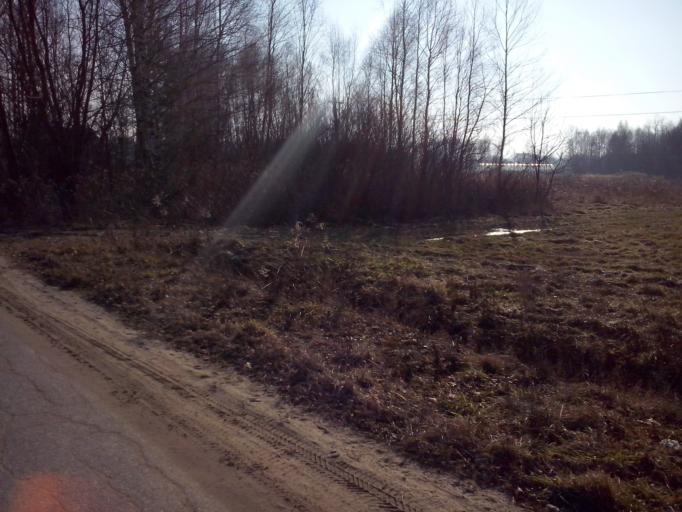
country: PL
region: Subcarpathian Voivodeship
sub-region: Powiat nizanski
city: Krzeszow
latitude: 50.4184
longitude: 22.3481
